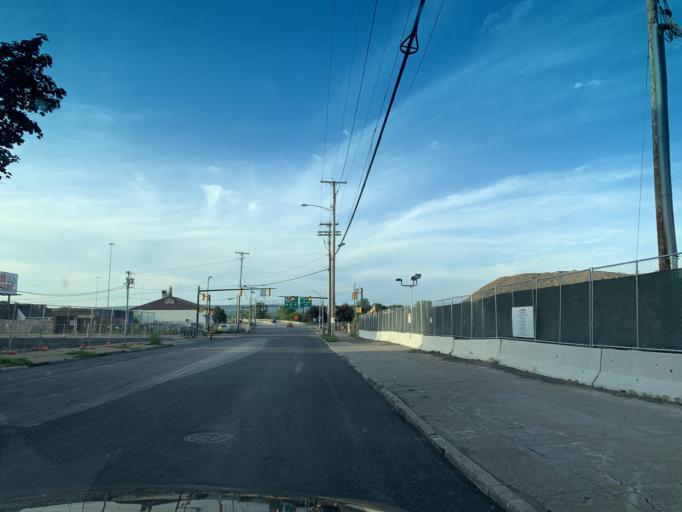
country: US
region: New York
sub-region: Oneida County
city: Utica
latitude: 43.1037
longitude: -75.2380
